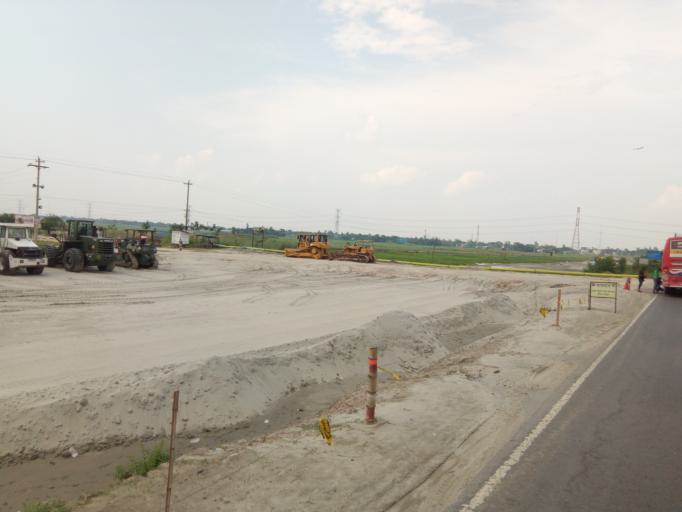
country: BD
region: Dhaka
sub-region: Dhaka
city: Dhaka
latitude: 23.6225
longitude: 90.3384
